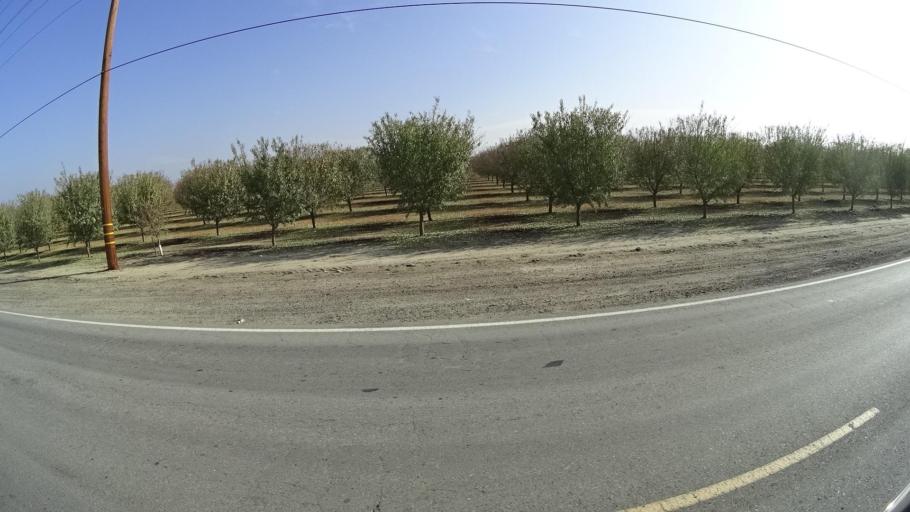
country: US
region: California
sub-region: Kern County
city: McFarland
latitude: 35.7201
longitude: -119.2231
